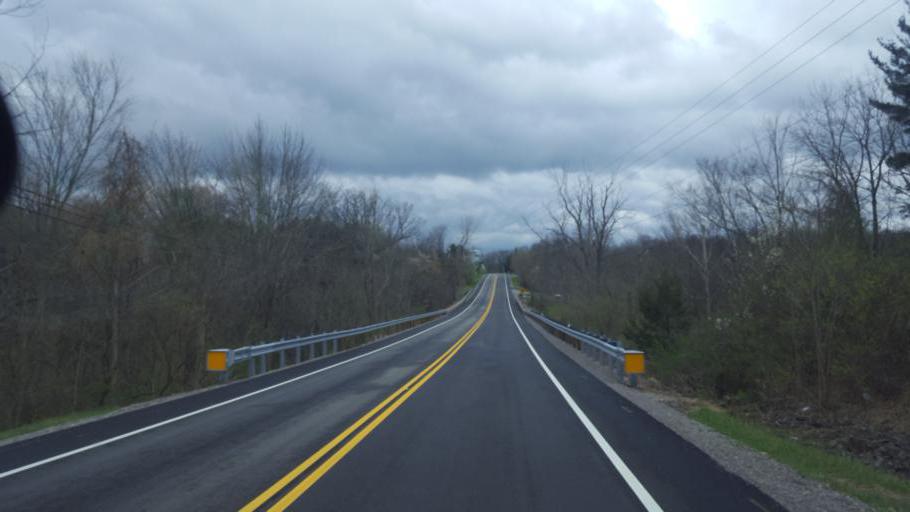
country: US
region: Ohio
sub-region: Delaware County
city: Sunbury
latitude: 40.1985
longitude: -82.8953
